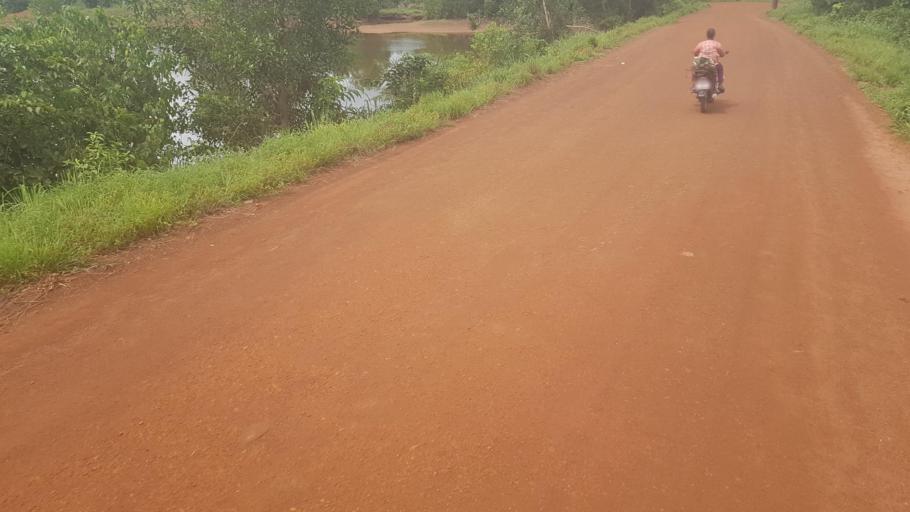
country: SL
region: Southern Province
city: Mogbwemo
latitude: 7.7547
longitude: -12.3075
